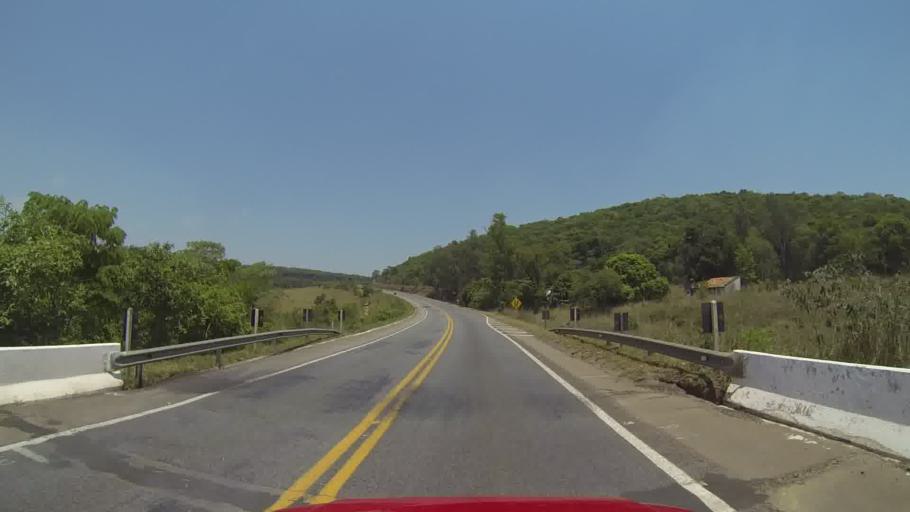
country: BR
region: Minas Gerais
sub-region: Itapecerica
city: Itapecerica
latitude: -20.2838
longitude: -45.1483
